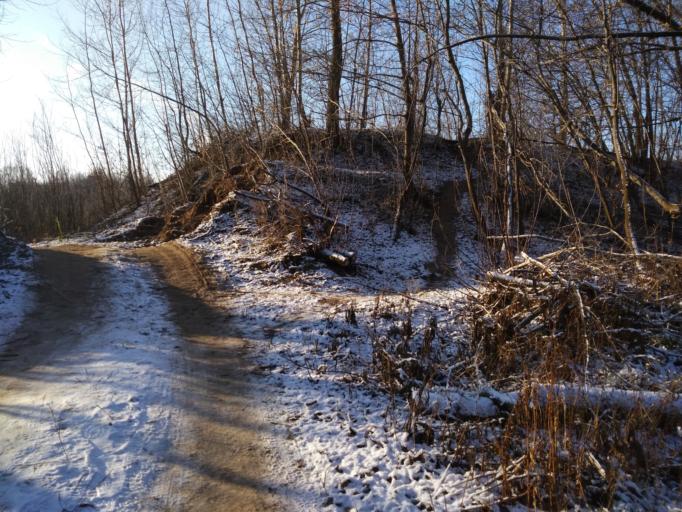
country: RU
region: Kirov
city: Vyatskiye Polyany
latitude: 56.2379
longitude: 51.0753
